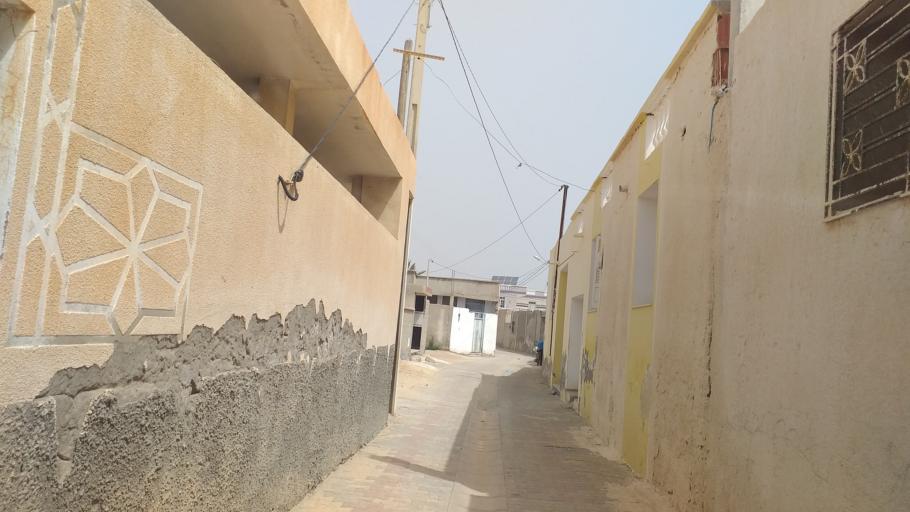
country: TN
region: Qabis
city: Gabes
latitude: 33.9428
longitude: 10.0623
